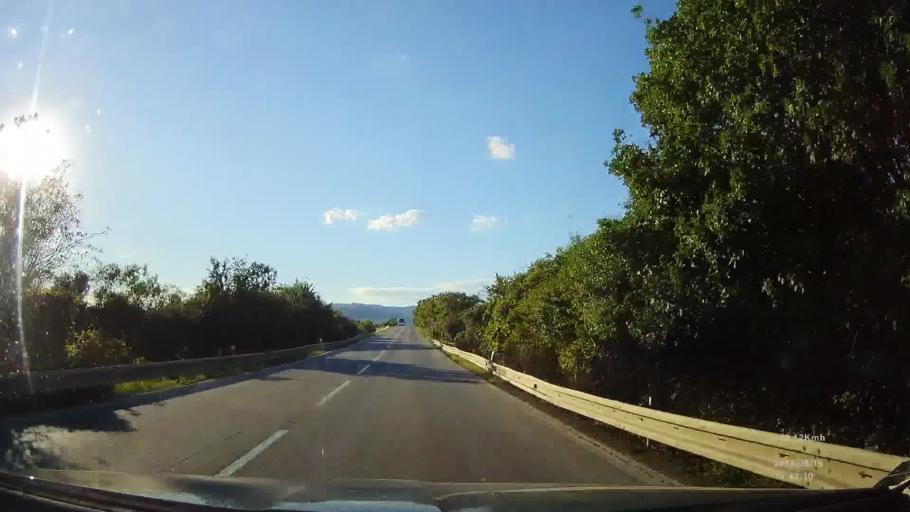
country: SK
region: Kosicky
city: Secovce
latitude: 48.7149
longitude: 21.6151
